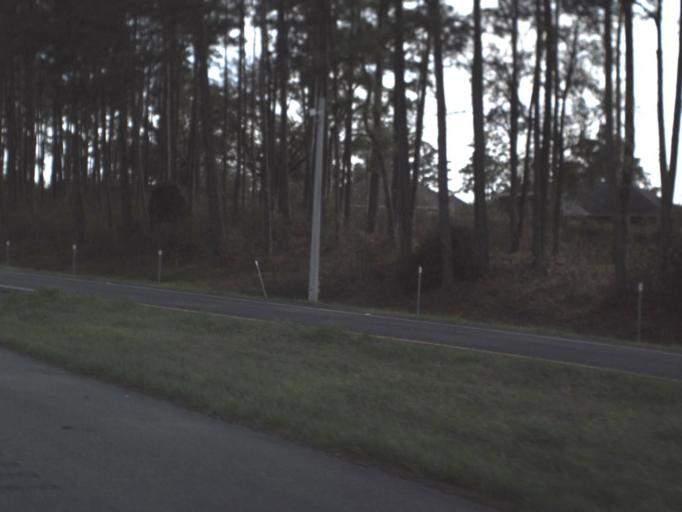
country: US
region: Florida
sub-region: Leon County
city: Tallahassee
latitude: 30.4822
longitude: -84.1541
